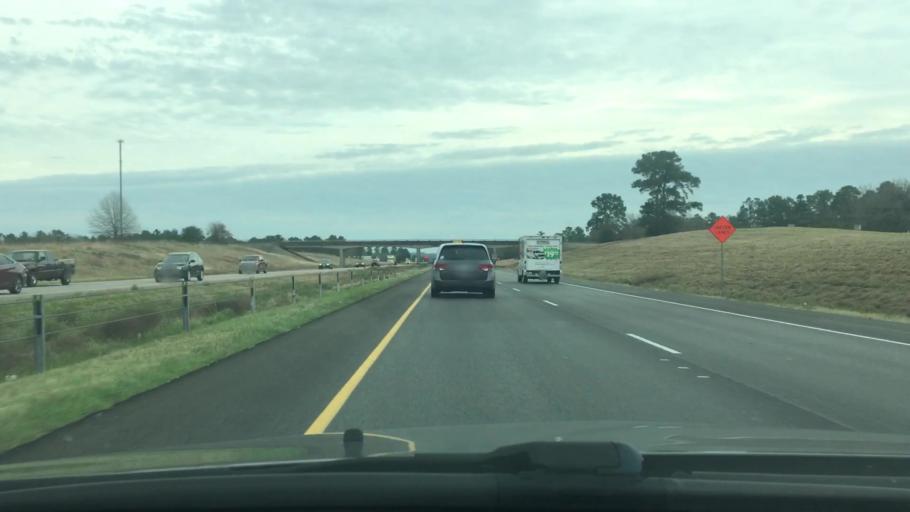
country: US
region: Texas
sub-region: Madison County
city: Madisonville
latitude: 30.8751
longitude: -95.7618
